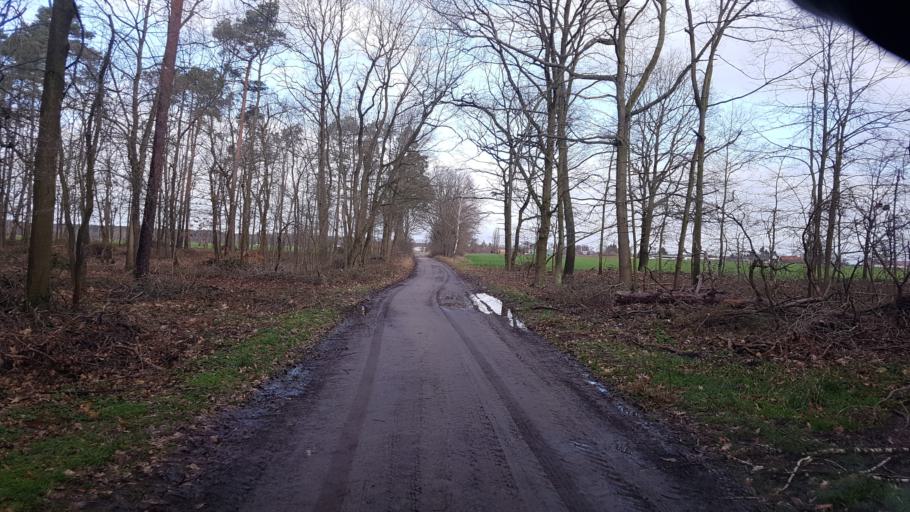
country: DE
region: Brandenburg
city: Finsterwalde
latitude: 51.5966
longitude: 13.6717
